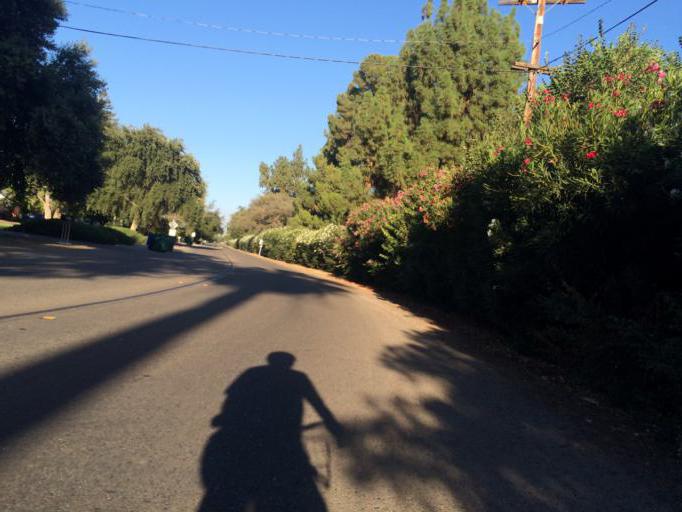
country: US
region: California
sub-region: Fresno County
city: Sunnyside
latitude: 36.7290
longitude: -119.6942
